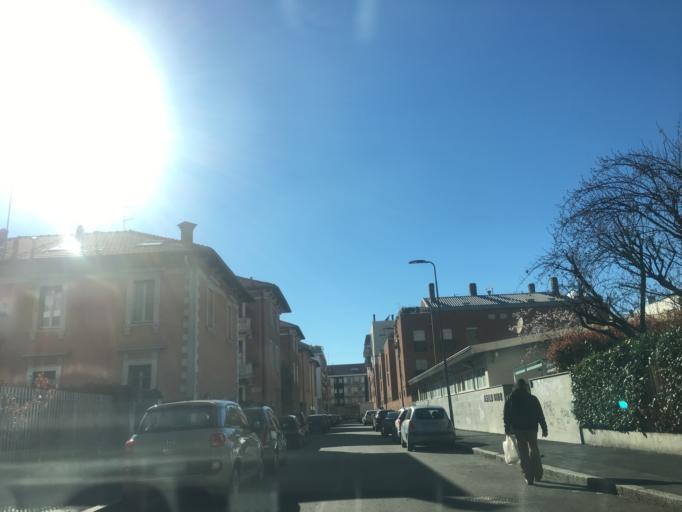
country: IT
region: Lombardy
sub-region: Citta metropolitana di Milano
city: Romano Banco
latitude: 45.4640
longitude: 9.1319
